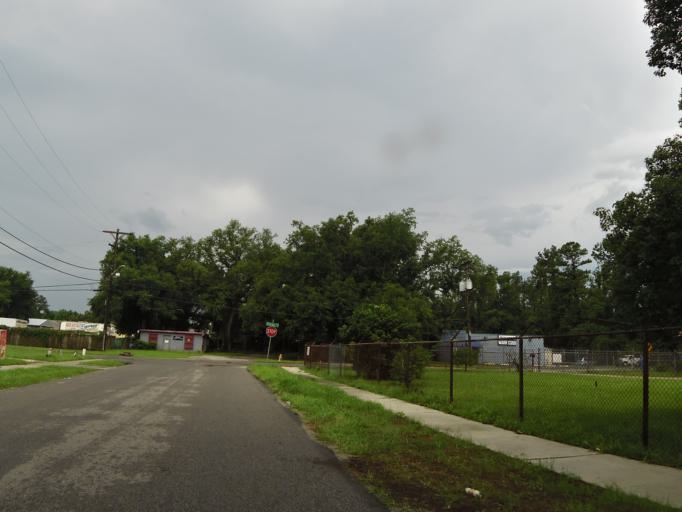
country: US
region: Florida
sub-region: Duval County
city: Jacksonville
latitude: 30.2772
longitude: -81.6385
